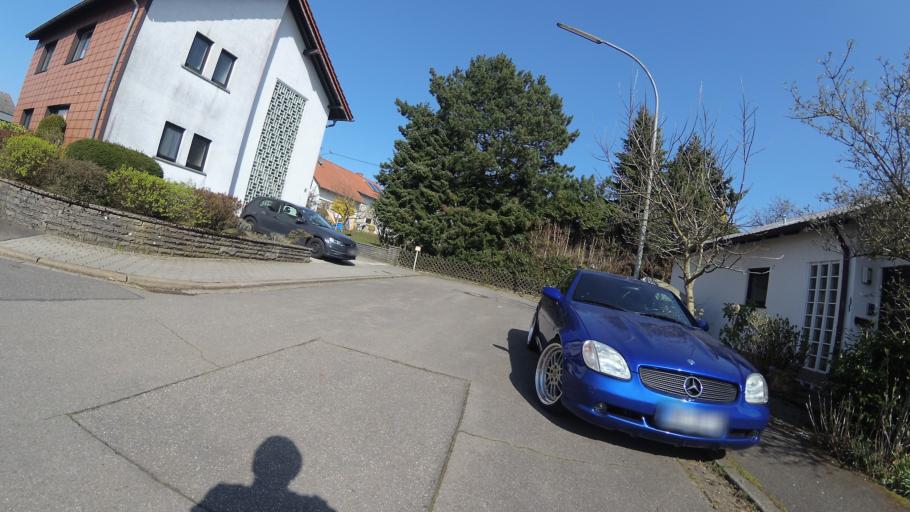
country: DE
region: Saarland
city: Merchweiler
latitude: 49.3464
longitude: 7.0075
